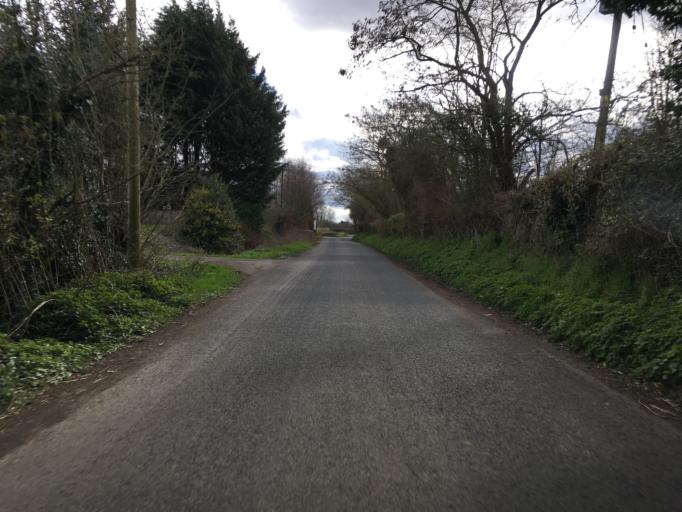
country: GB
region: England
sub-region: Gloucestershire
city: Mitcheldean
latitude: 51.8266
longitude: -2.4051
